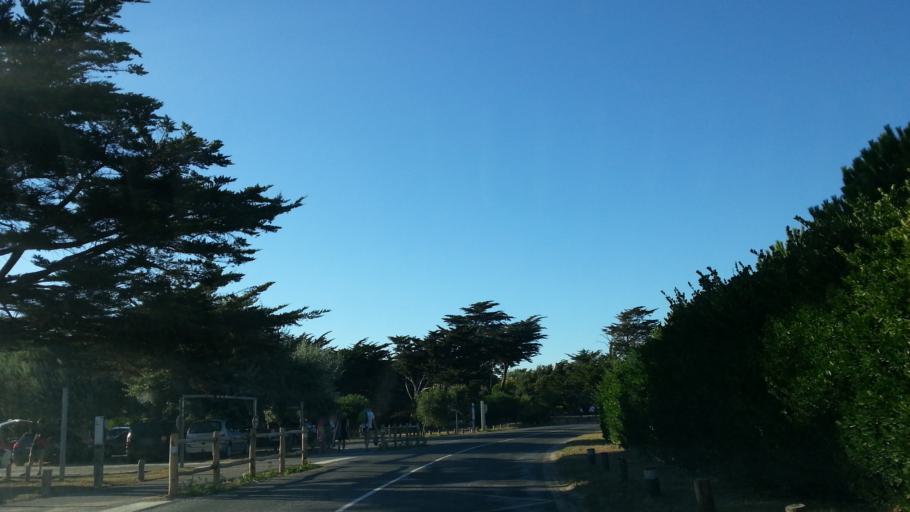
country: FR
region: Poitou-Charentes
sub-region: Departement de la Charente-Maritime
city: Dolus-d'Oleron
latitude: 45.8964
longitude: -1.2878
